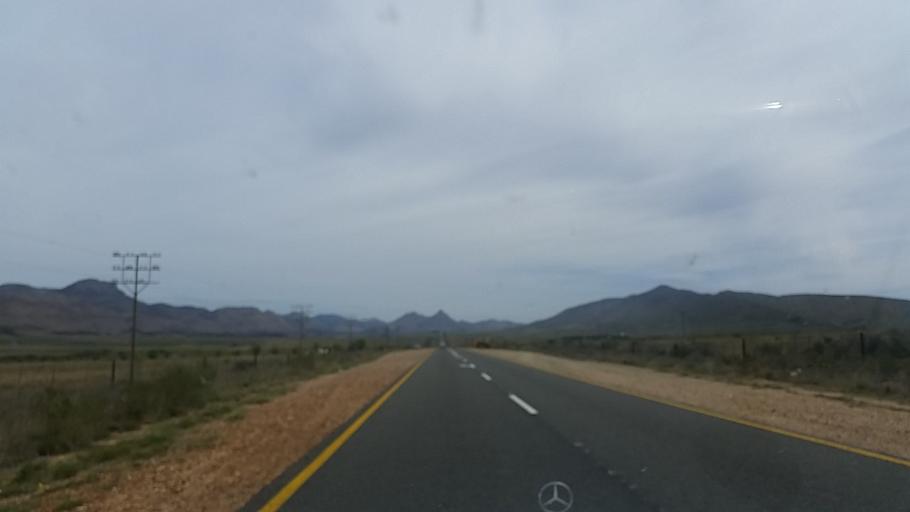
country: ZA
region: Western Cape
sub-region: Eden District Municipality
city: George
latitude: -33.8033
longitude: 22.5755
